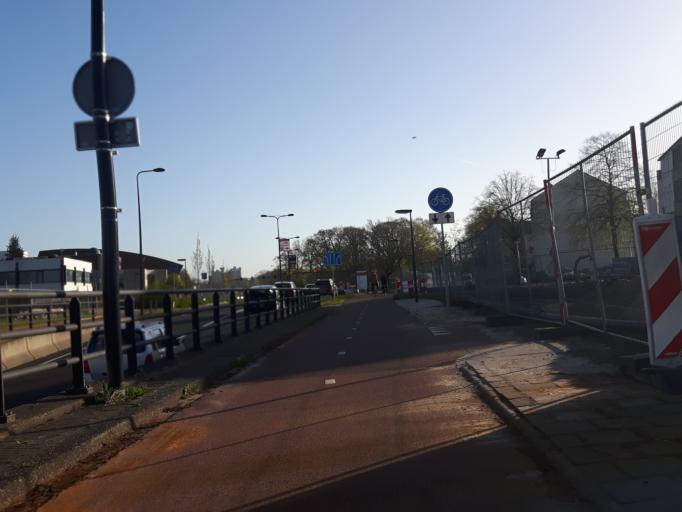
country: NL
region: Overijssel
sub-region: Gemeente Enschede
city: Enschede
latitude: 52.2340
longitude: 6.8451
